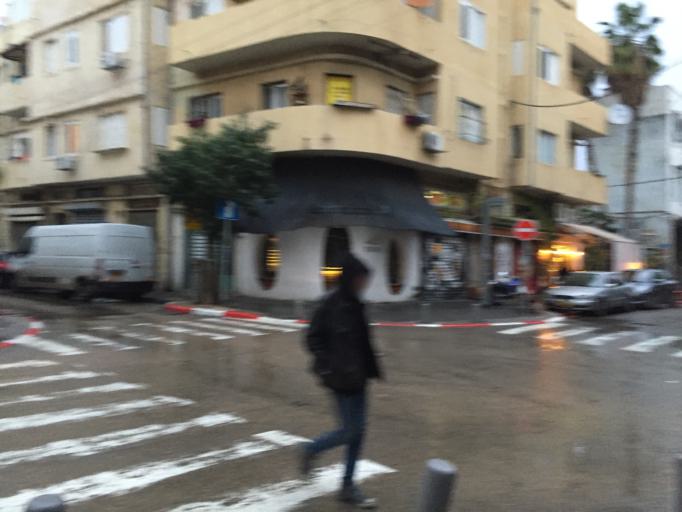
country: IL
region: Tel Aviv
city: Yafo
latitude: 32.0571
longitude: 34.7700
